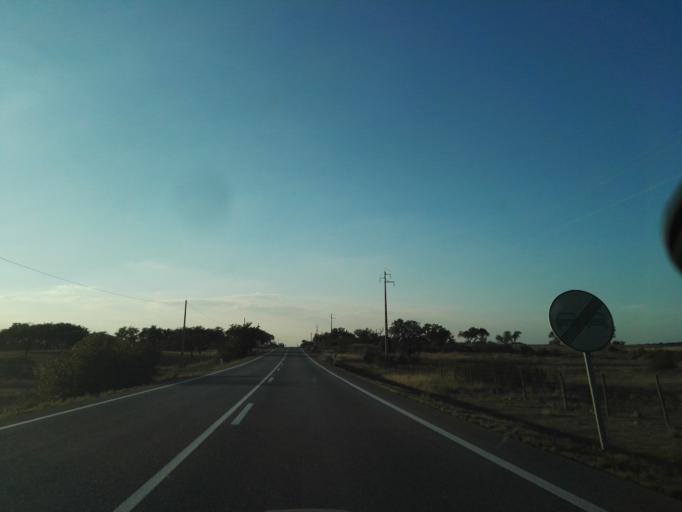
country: PT
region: Evora
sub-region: Arraiolos
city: Arraiolos
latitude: 38.8471
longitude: -7.8879
